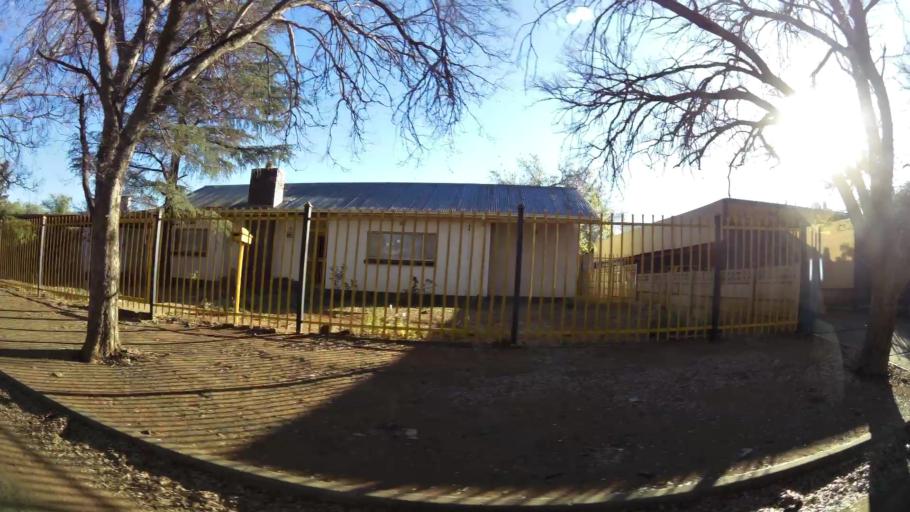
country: ZA
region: Northern Cape
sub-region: Frances Baard District Municipality
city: Kimberley
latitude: -28.7406
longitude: 24.7411
